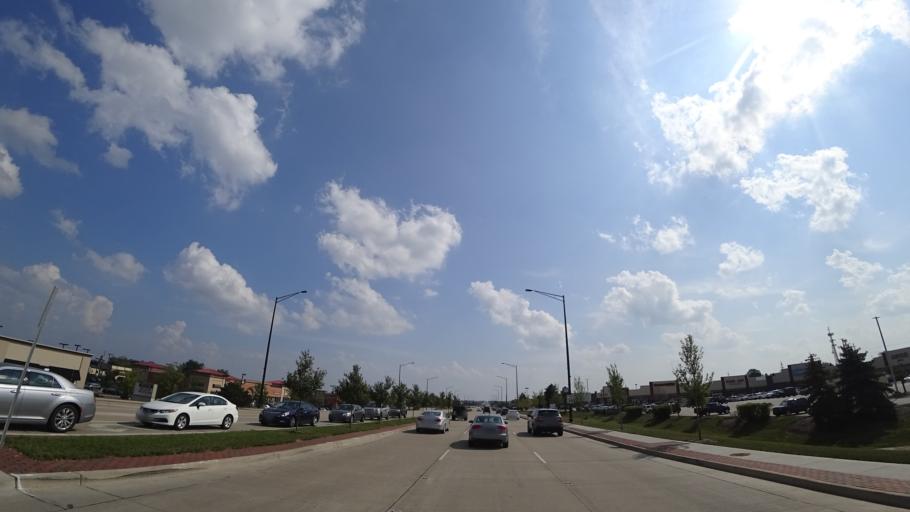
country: US
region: Illinois
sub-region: Cook County
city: Orland Park
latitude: 41.6196
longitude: -87.8537
